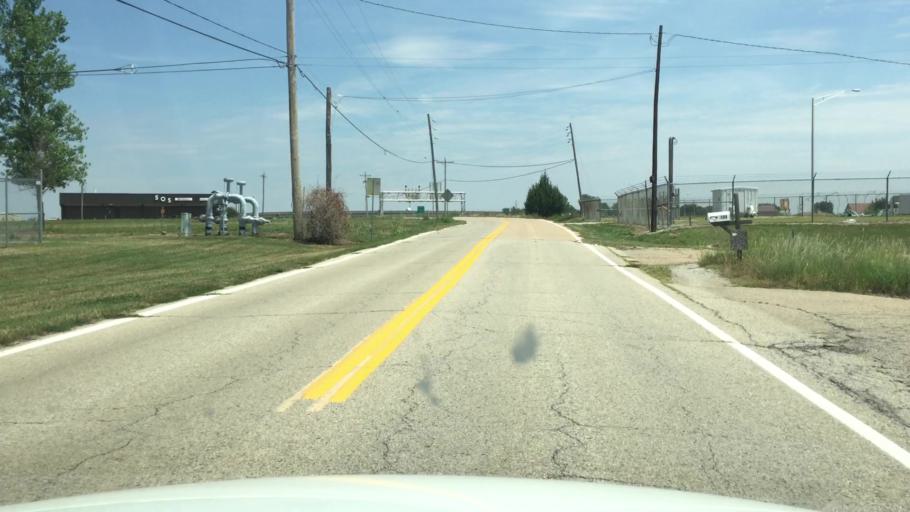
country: US
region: Kansas
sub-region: Shawnee County
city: Topeka
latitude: 39.0297
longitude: -95.6190
